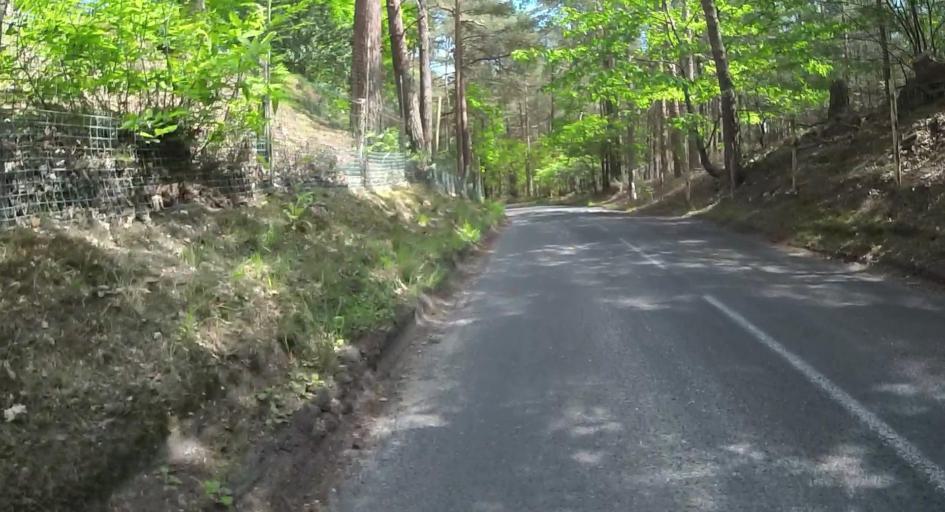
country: GB
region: England
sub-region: Surrey
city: Farnham
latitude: 51.1868
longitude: -0.7846
